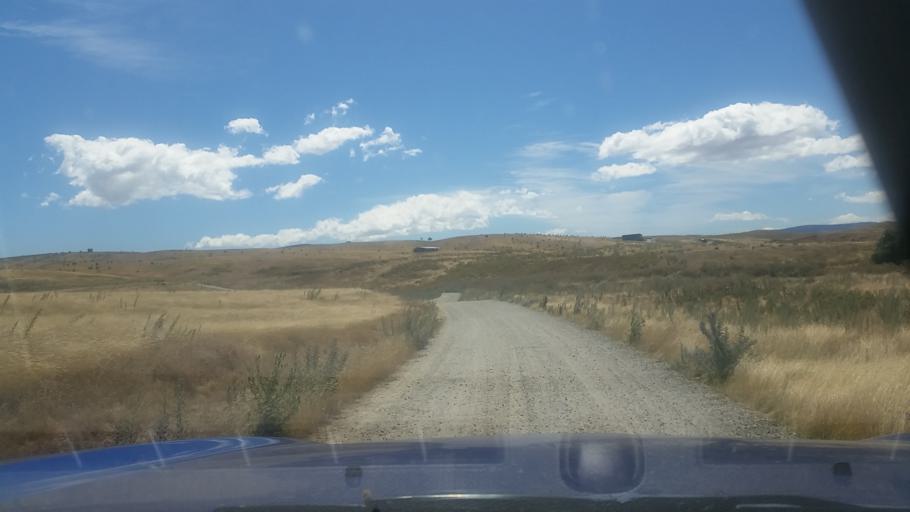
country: NZ
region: Otago
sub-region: Queenstown-Lakes District
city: Wanaka
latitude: -45.1955
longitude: 169.4119
